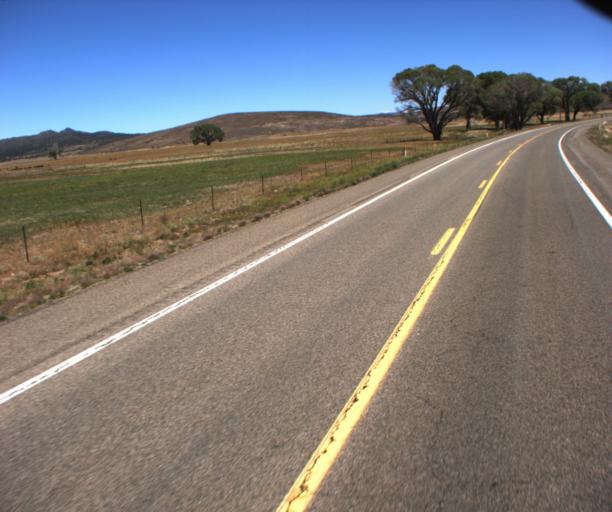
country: US
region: Arizona
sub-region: Yavapai County
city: Congress
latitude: 34.2965
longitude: -112.7231
